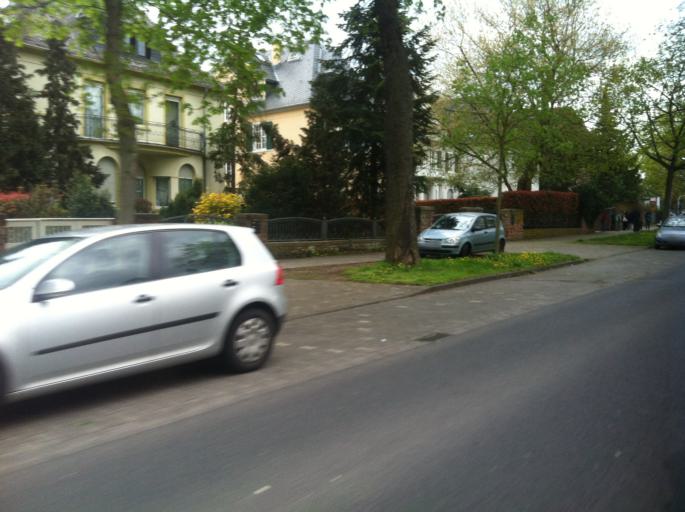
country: DE
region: Rheinland-Pfalz
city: Mainz
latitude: 49.9895
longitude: 8.2793
